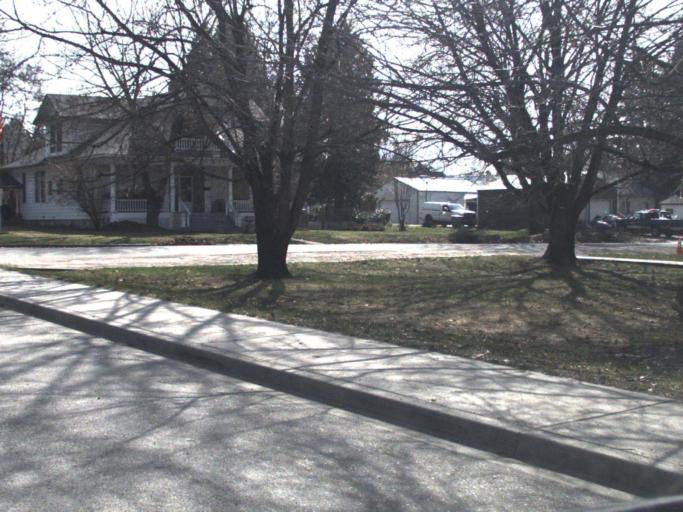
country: US
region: Washington
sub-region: Stevens County
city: Colville
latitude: 48.5466
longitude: -117.9017
